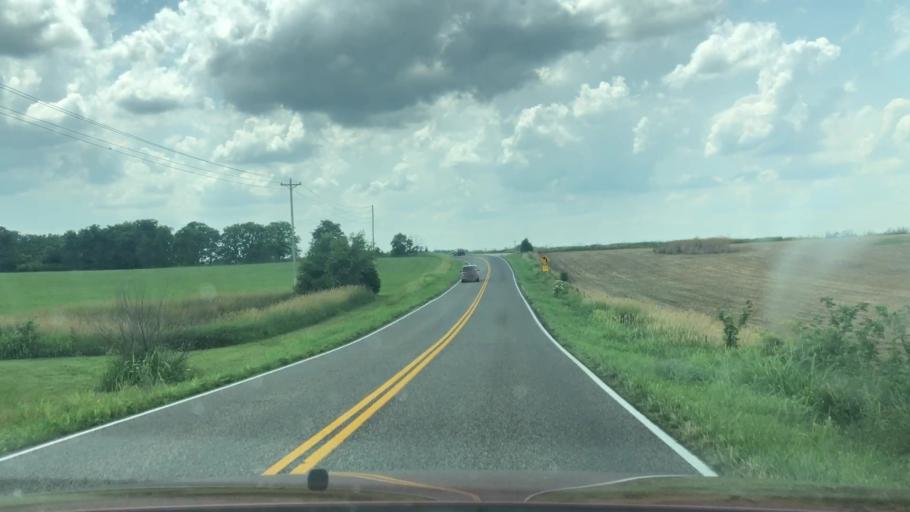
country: US
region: Missouri
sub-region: Christian County
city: Ozark
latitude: 36.9432
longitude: -93.2470
